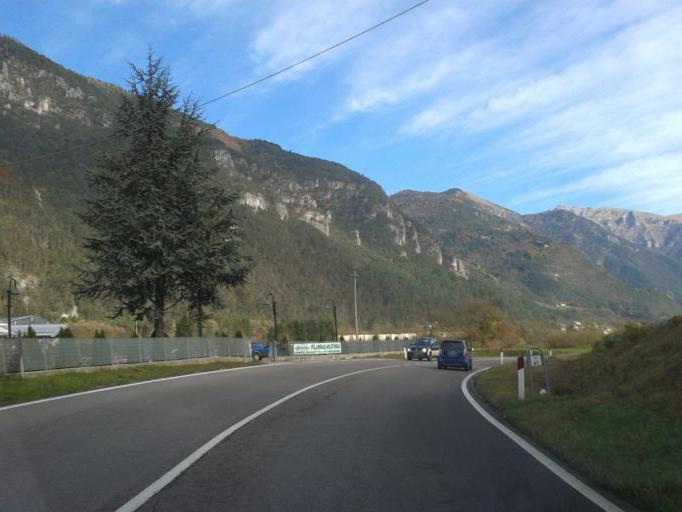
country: IT
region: Trentino-Alto Adige
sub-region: Provincia di Trento
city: Bolbeno
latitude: 46.0363
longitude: 10.7379
